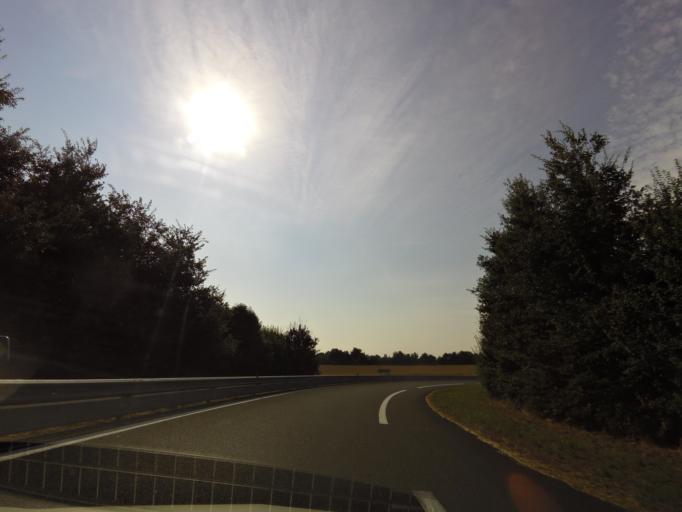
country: FR
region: Pays de la Loire
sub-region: Departement de la Vendee
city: Les Essarts
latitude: 46.8086
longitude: -1.2057
